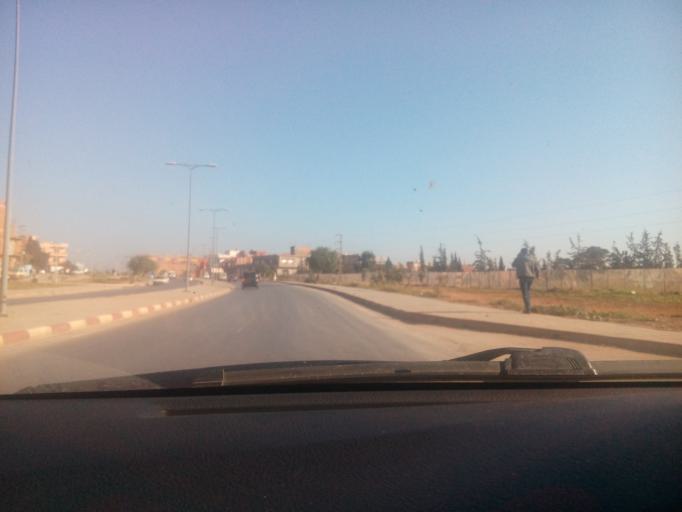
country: DZ
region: Oran
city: Oran
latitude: 35.6623
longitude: -0.6855
